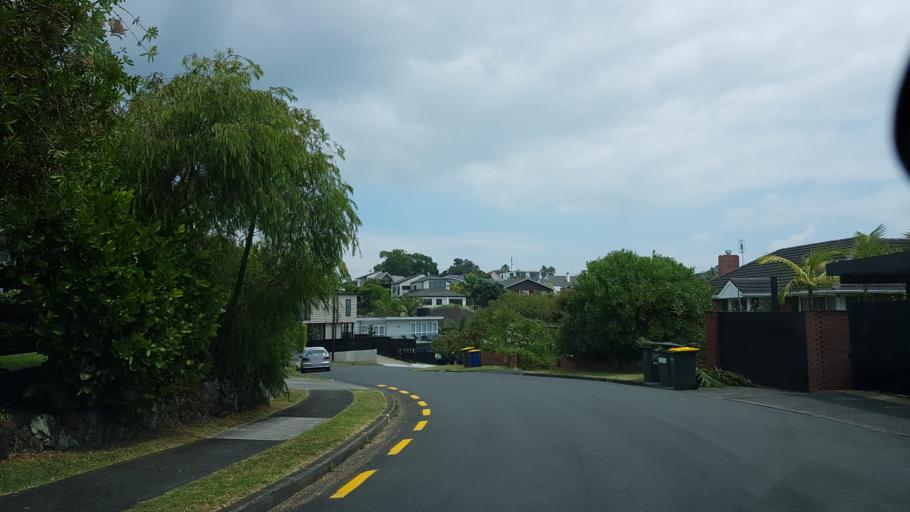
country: NZ
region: Auckland
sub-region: Auckland
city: North Shore
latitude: -36.7960
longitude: 174.7831
